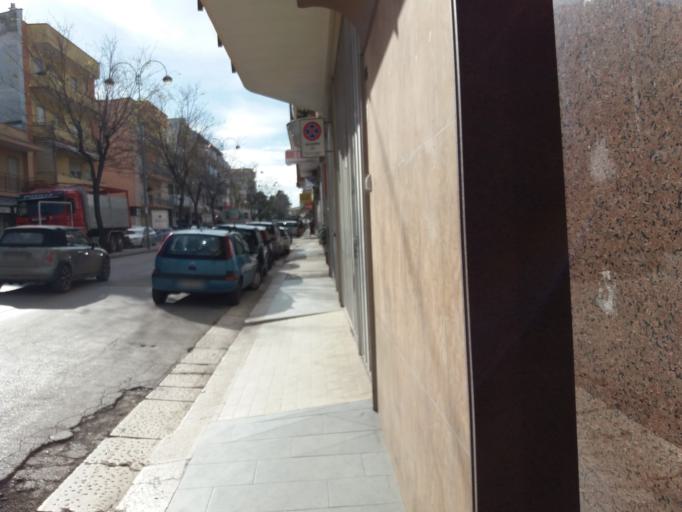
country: IT
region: Apulia
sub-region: Provincia di Barletta - Andria - Trani
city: Andria
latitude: 41.2219
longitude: 16.3065
